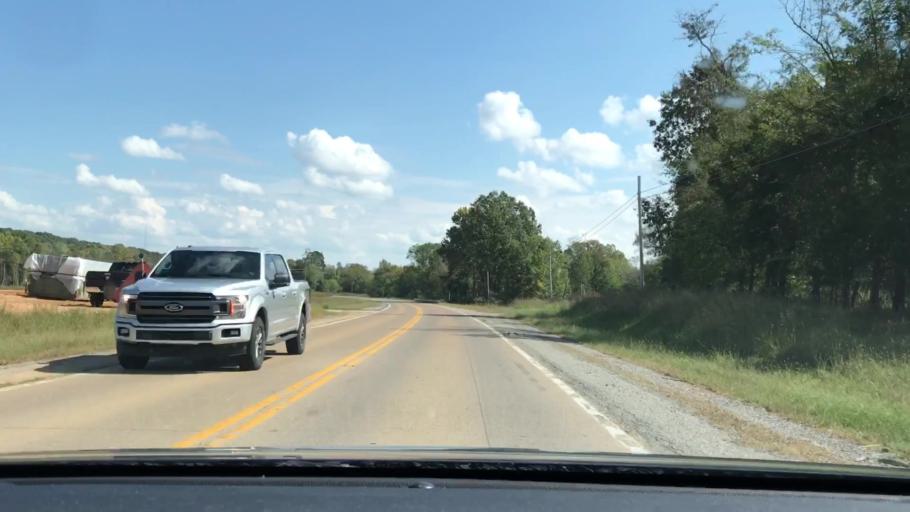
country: US
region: Kentucky
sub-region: Trigg County
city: Cadiz
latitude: 36.7988
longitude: -87.9451
